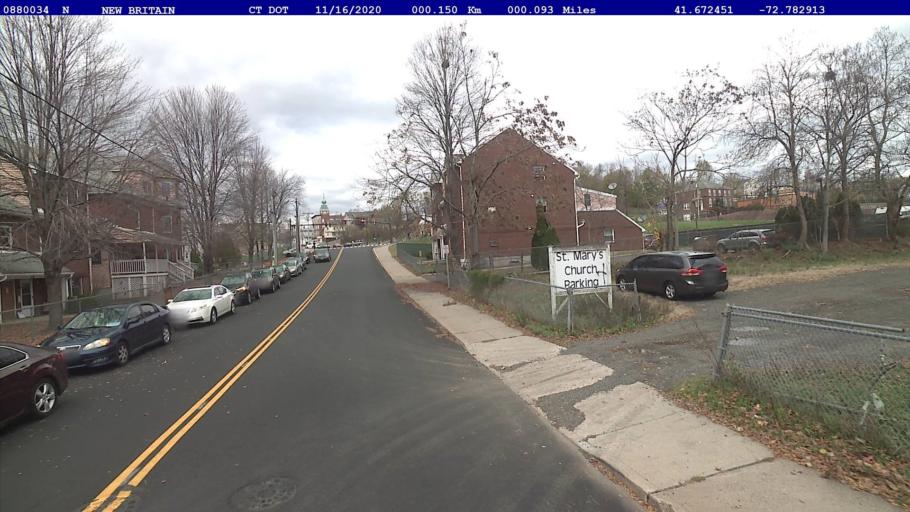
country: US
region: Connecticut
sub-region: Hartford County
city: New Britain
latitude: 41.6724
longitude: -72.7829
